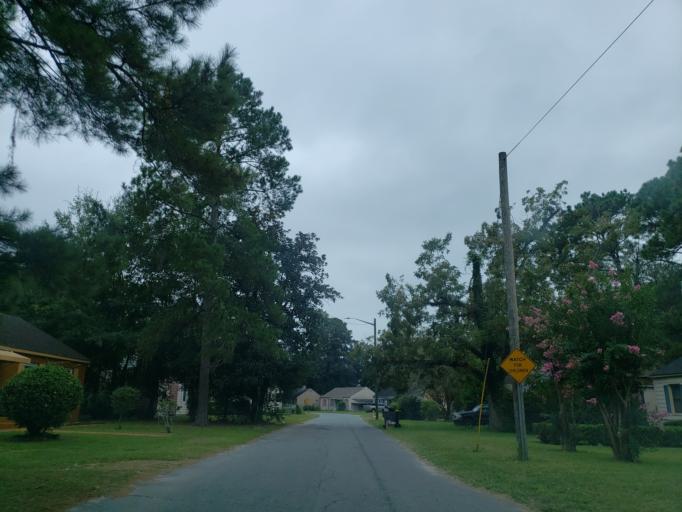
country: US
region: Georgia
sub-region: Chatham County
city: Thunderbolt
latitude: 32.0471
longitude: -81.0729
